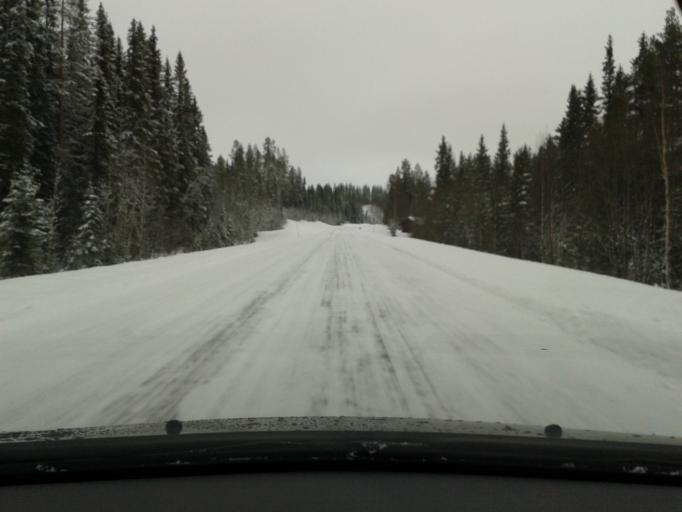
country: SE
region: Vaesterbotten
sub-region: Vilhelmina Kommun
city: Sjoberg
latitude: 64.9538
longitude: 15.8618
